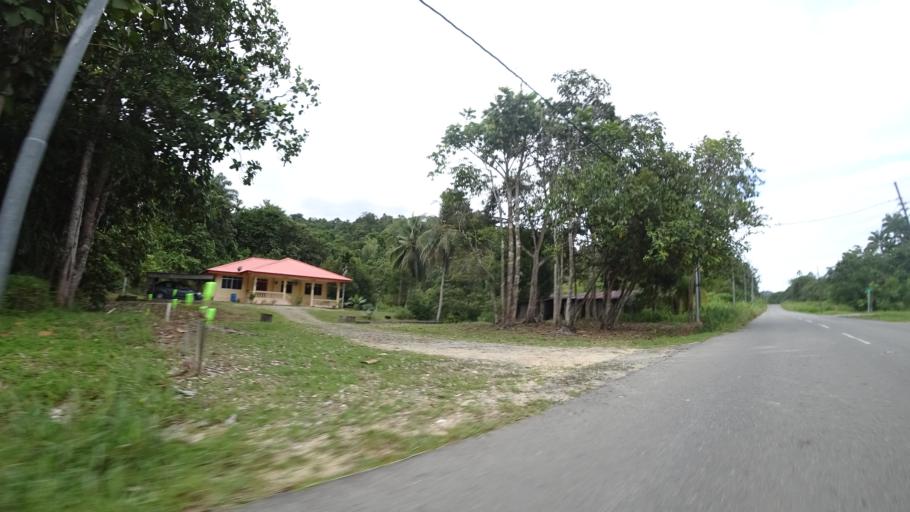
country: BN
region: Brunei and Muara
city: Bandar Seri Begawan
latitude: 4.8478
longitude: 114.9533
